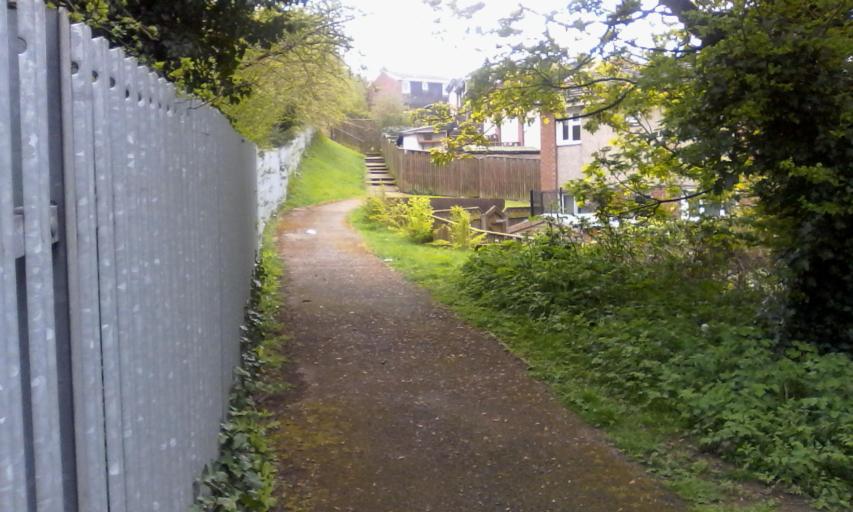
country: GB
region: England
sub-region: Nottingham
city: Nottingham
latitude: 52.9691
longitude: -1.1232
